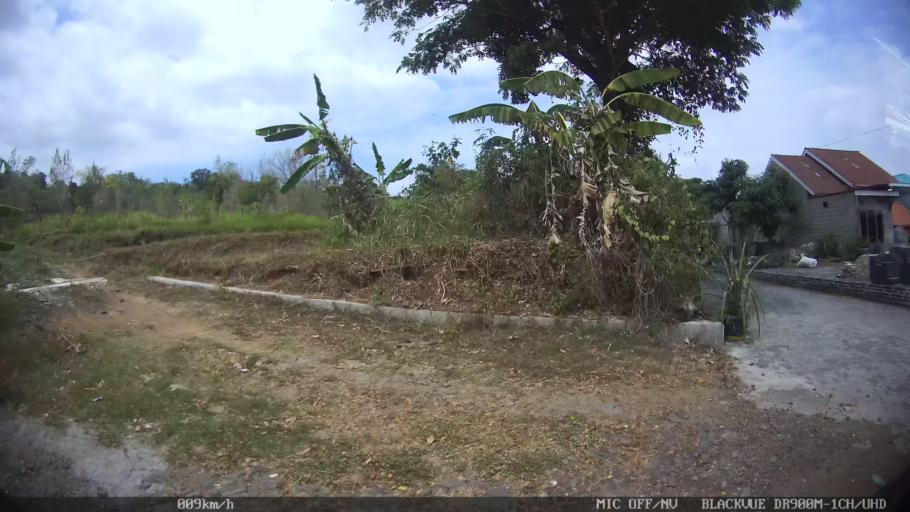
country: ID
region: Central Java
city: Candi Prambanan
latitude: -7.7841
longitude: 110.4985
